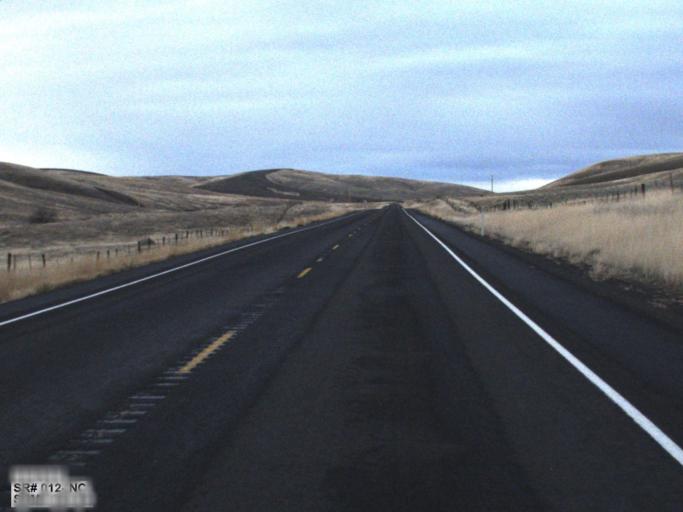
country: US
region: Washington
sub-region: Columbia County
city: Dayton
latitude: 46.5122
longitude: -117.9459
